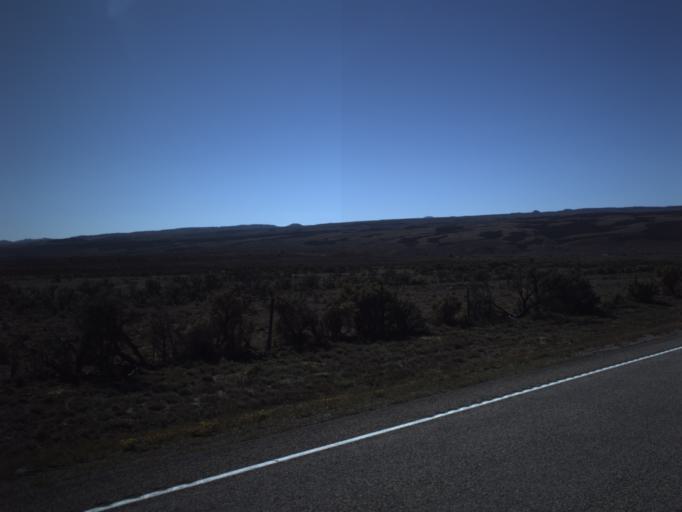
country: US
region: Utah
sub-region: Garfield County
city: Panguitch
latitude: 37.7460
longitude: -112.3466
